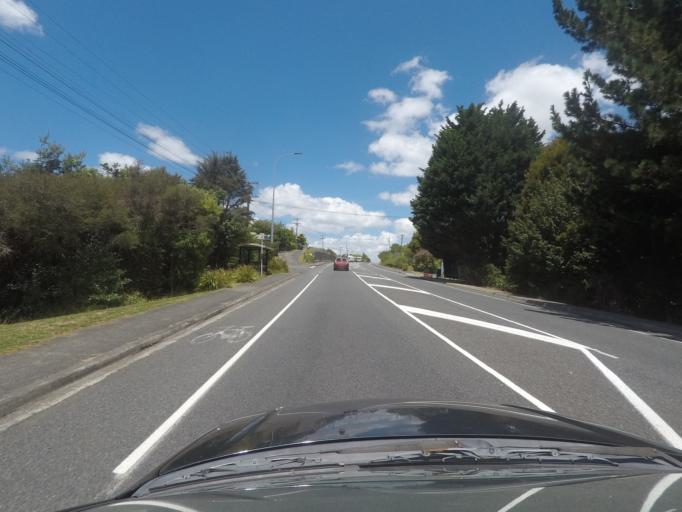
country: NZ
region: Northland
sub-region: Whangarei
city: Whangarei
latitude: -35.7457
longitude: 174.3669
